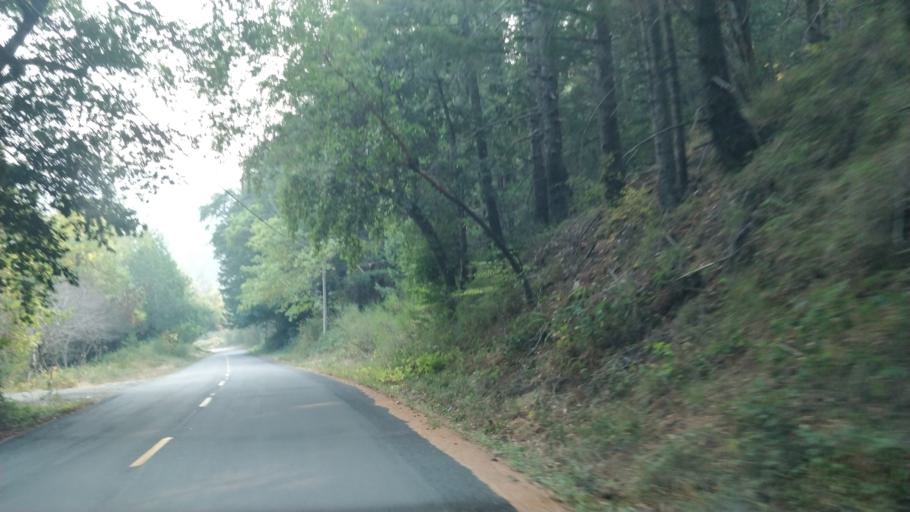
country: US
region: California
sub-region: Humboldt County
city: Rio Dell
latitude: 40.2878
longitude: -124.2530
